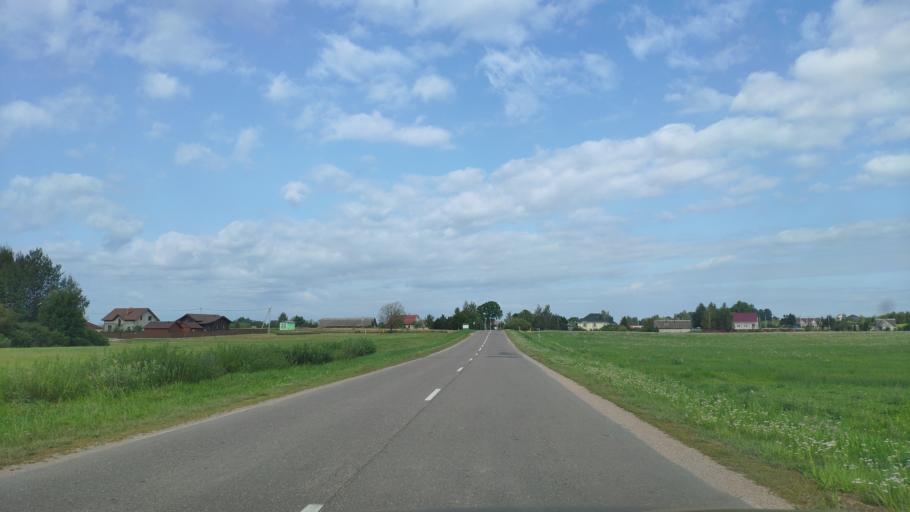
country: BY
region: Minsk
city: Khatsyezhyna
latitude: 53.8804
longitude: 27.2809
